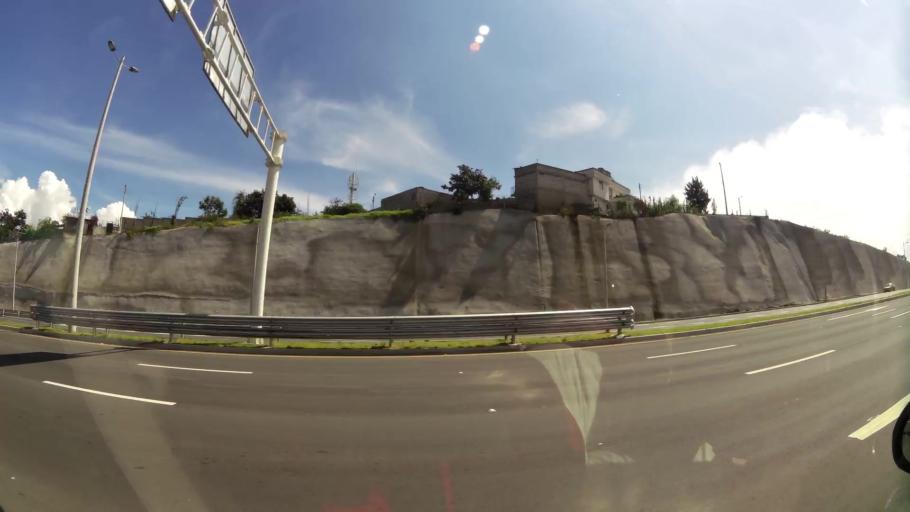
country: EC
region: Pichincha
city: Sangolqui
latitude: -0.2198
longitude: -78.3901
